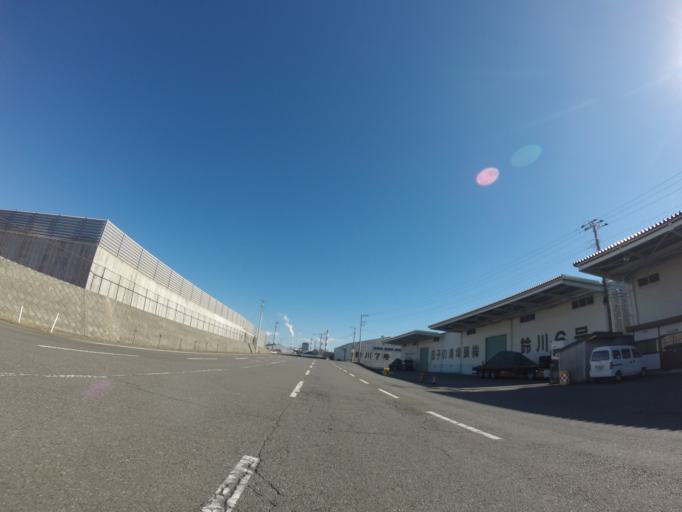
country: JP
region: Shizuoka
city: Fuji
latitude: 35.1454
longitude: 138.6983
